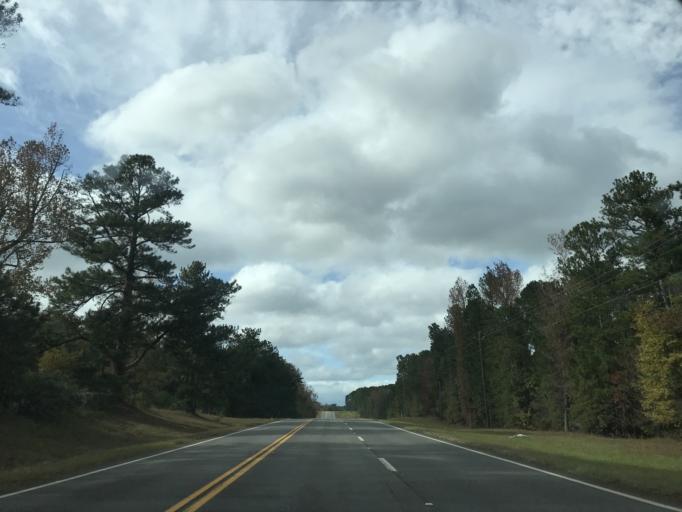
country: US
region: Georgia
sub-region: Jones County
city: Gray
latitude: 32.9697
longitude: -83.4883
